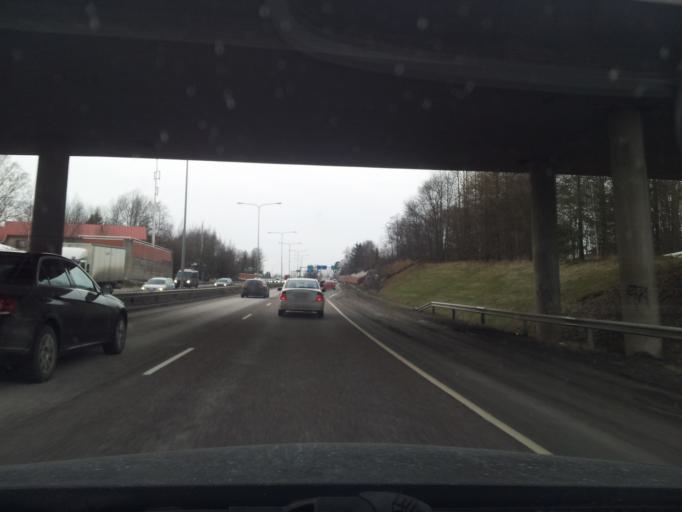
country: FI
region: Uusimaa
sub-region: Helsinki
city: Helsinki
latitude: 60.2446
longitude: 24.9588
